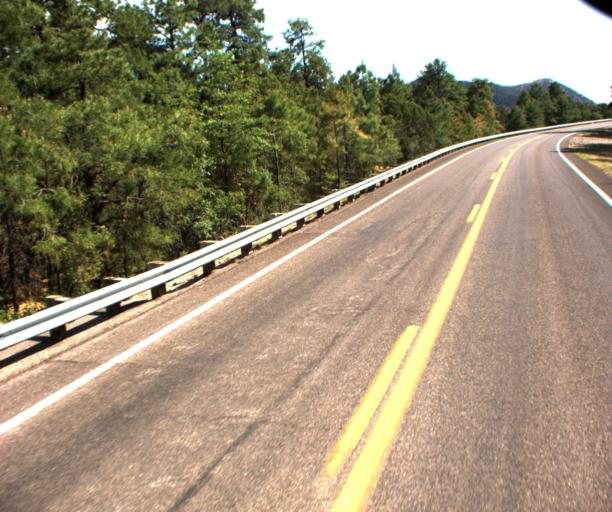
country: US
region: Arizona
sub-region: Greenlee County
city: Clifton
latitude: 33.0568
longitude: -109.0813
